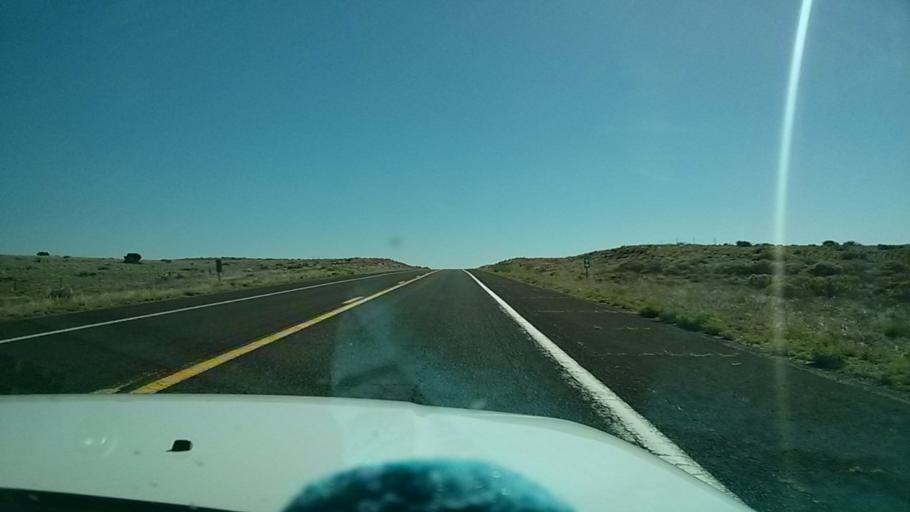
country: US
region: Arizona
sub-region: Mohave County
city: Peach Springs
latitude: 35.5159
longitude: -113.4992
